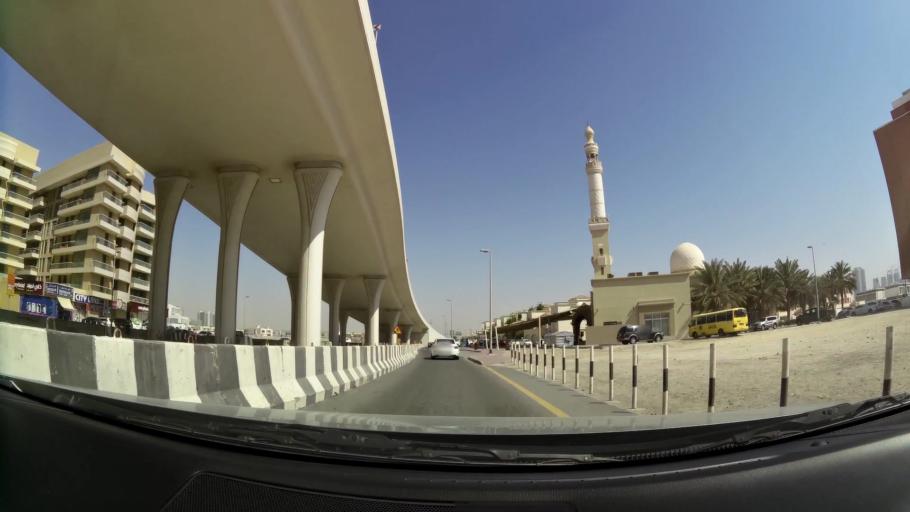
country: AE
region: Dubai
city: Dubai
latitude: 25.1119
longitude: 55.1880
